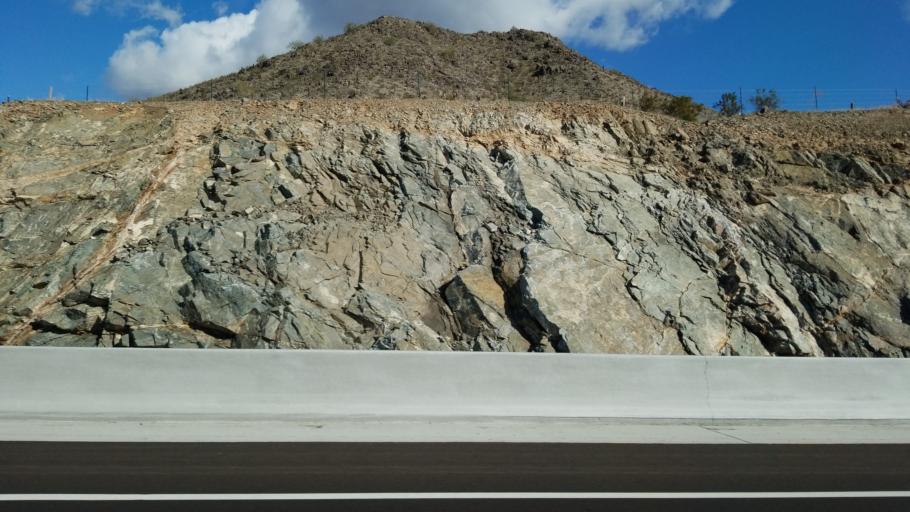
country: US
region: Arizona
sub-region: Maricopa County
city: Laveen
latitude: 33.3225
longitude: -112.1643
